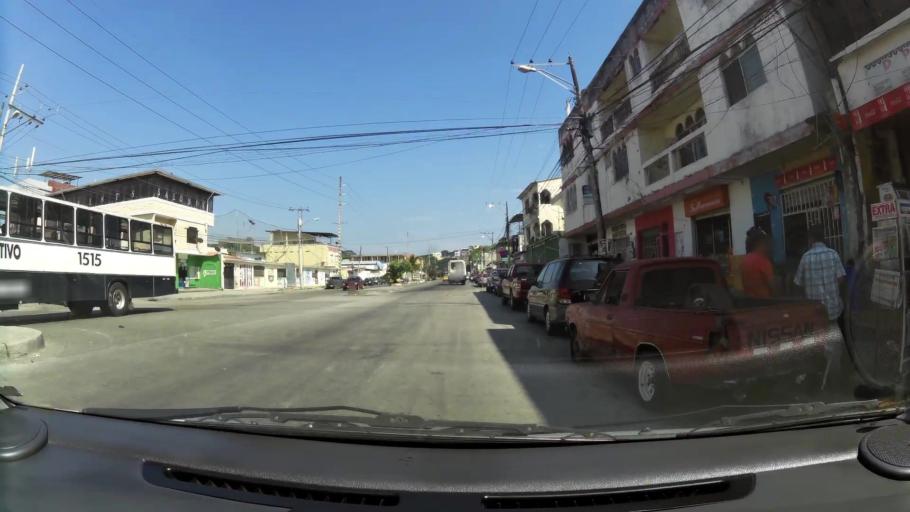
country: EC
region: Guayas
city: Eloy Alfaro
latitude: -2.1314
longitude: -79.9102
